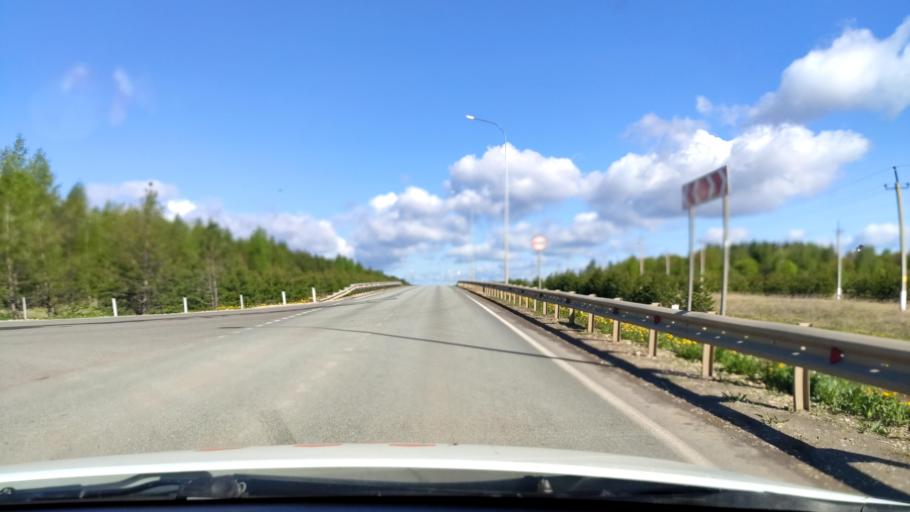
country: RU
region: Tatarstan
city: Sviyazhsk
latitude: 55.7303
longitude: 48.7437
